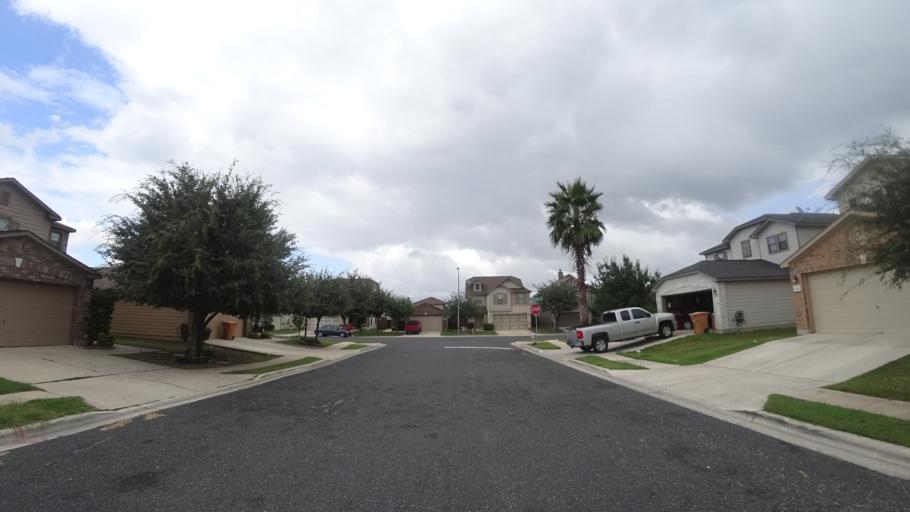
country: US
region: Texas
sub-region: Travis County
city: Onion Creek
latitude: 30.1498
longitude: -97.7426
